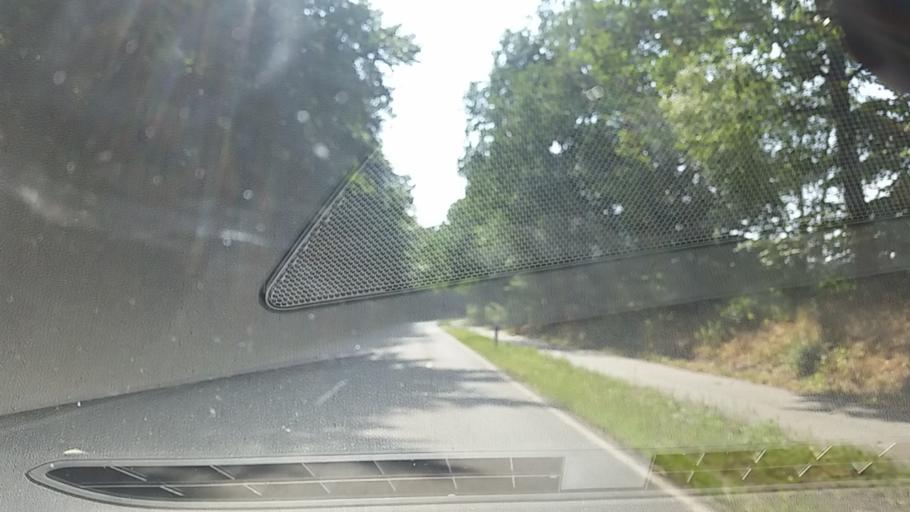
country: DE
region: Schleswig-Holstein
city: Grande
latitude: 53.5748
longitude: 10.3688
